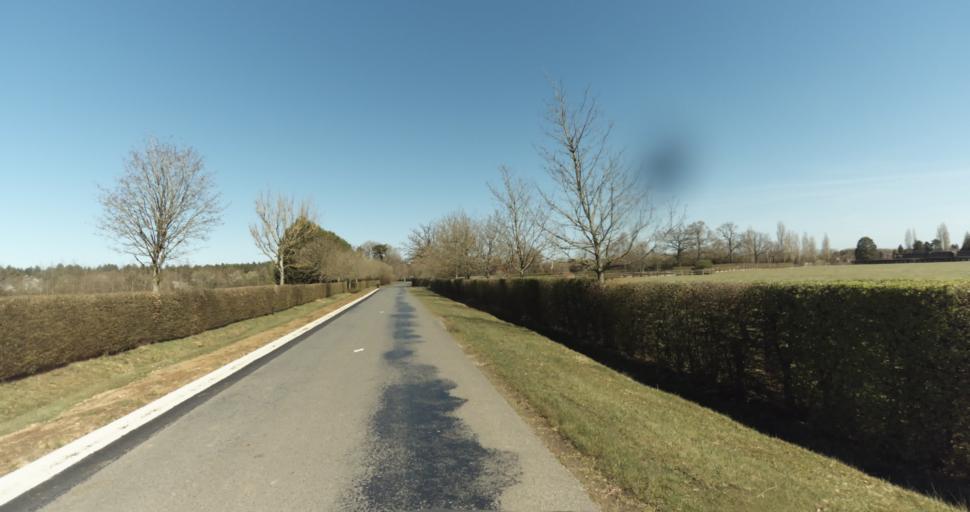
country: FR
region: Lower Normandy
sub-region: Departement du Calvados
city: Livarot
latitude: 48.9546
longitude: 0.0916
